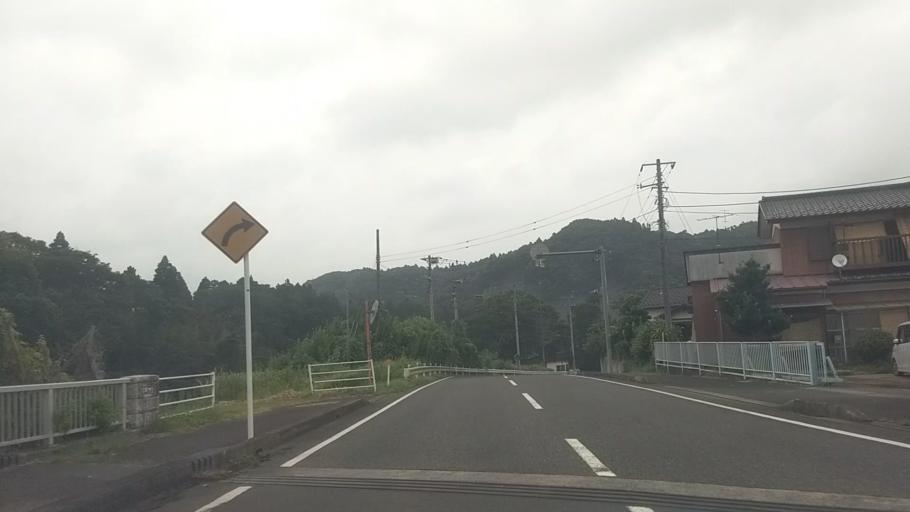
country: JP
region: Chiba
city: Ohara
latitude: 35.2679
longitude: 140.2540
